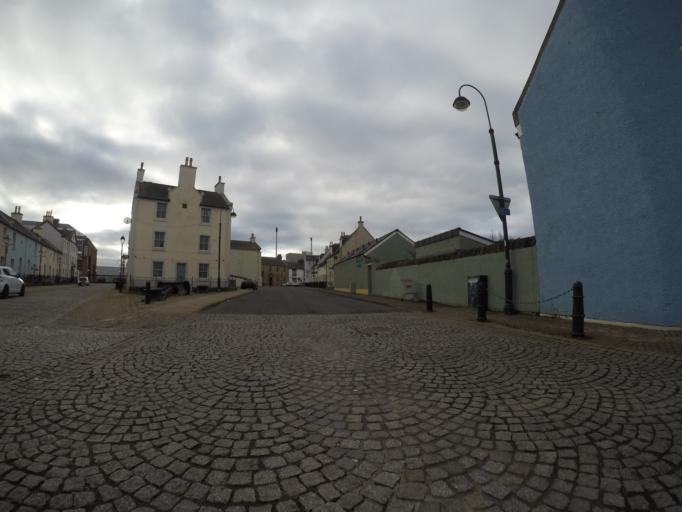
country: GB
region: Scotland
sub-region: North Ayrshire
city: Irvine
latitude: 55.6101
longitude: -4.6783
